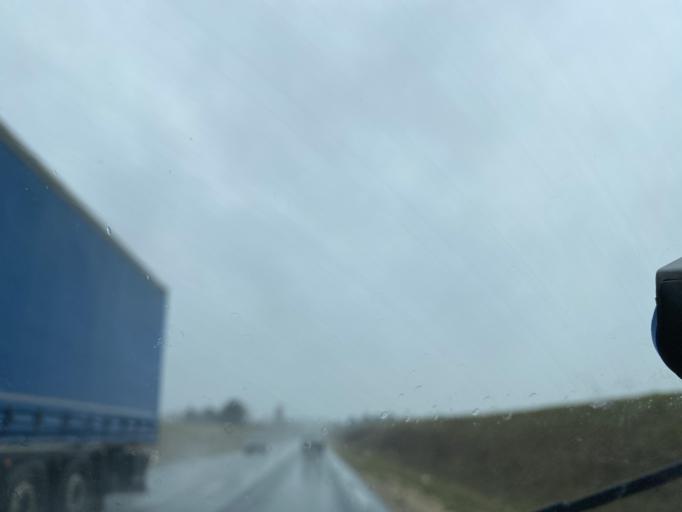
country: FR
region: Centre
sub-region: Departement d'Eure-et-Loir
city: Mainvilliers
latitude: 48.4597
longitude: 1.4535
